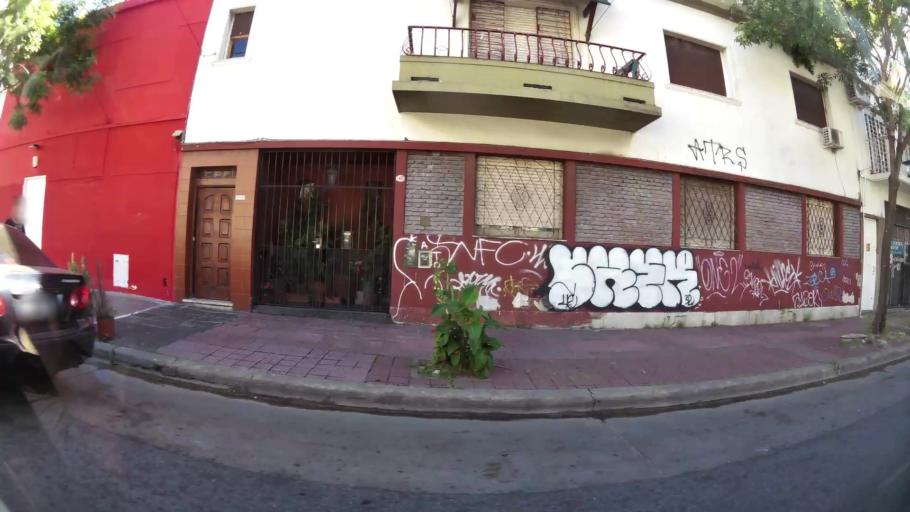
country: AR
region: Buenos Aires F.D.
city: Colegiales
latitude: -34.5569
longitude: -58.4790
